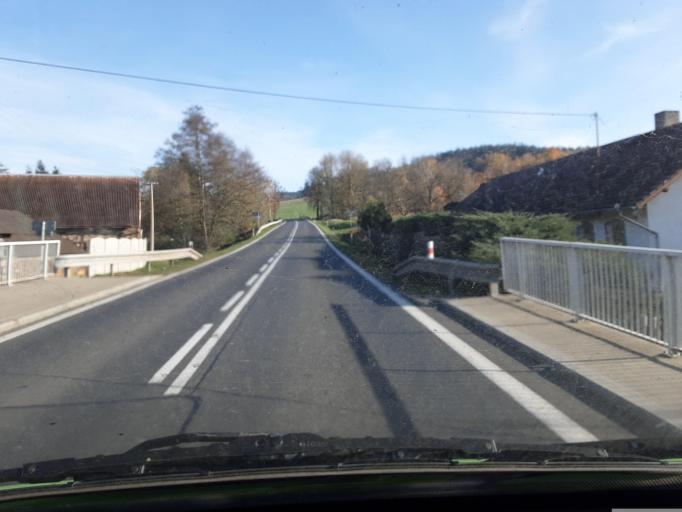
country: CZ
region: Plzensky
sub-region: Okres Klatovy
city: Kolinec
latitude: 49.3589
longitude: 13.3851
